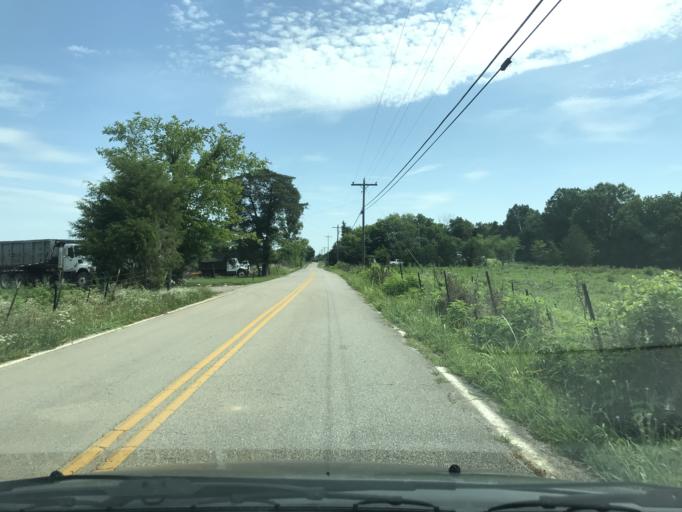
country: US
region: Tennessee
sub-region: Hamilton County
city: Lakesite
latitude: 35.1973
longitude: -85.0299
